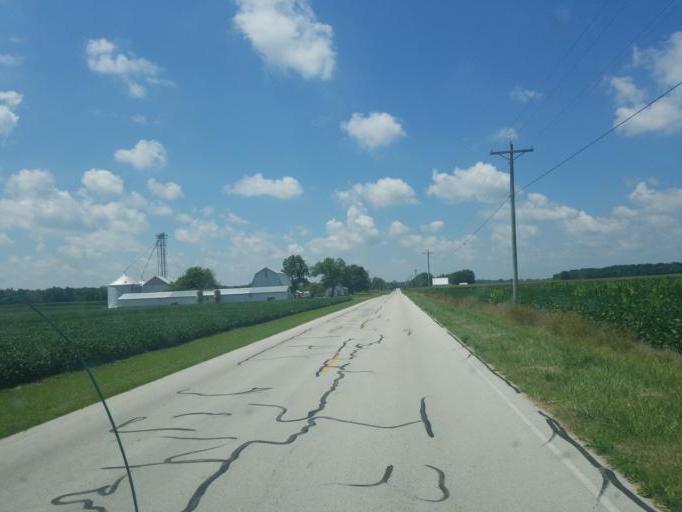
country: US
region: Ohio
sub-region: Allen County
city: Spencerville
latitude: 40.6771
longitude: -84.4909
